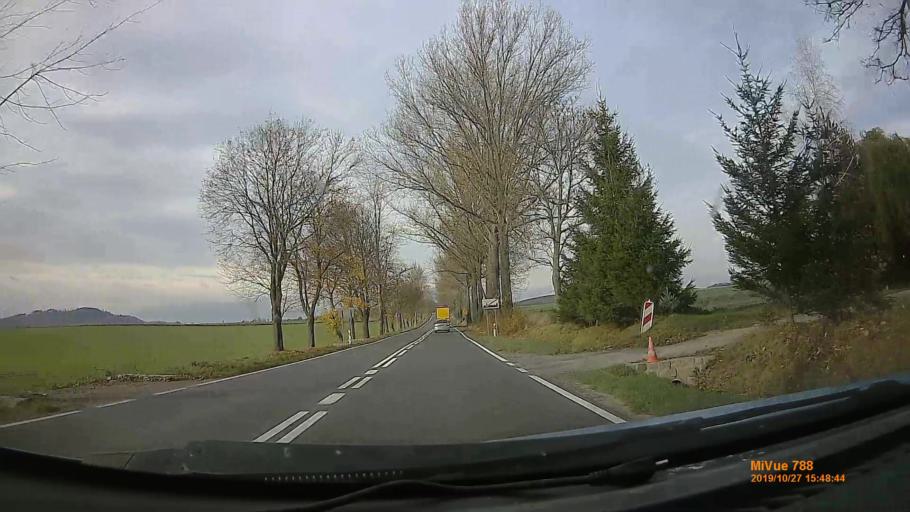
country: PL
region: Lower Silesian Voivodeship
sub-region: Powiat klodzki
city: Bozkow
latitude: 50.4999
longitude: 16.5850
